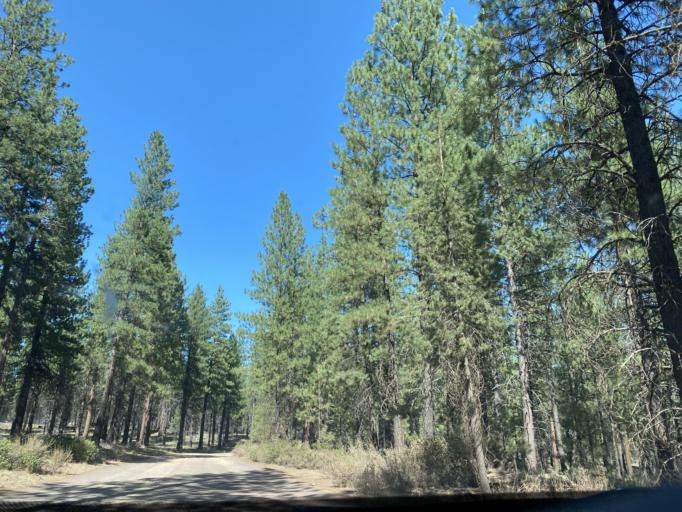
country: US
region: Oregon
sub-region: Deschutes County
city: Sunriver
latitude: 43.8698
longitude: -121.4827
